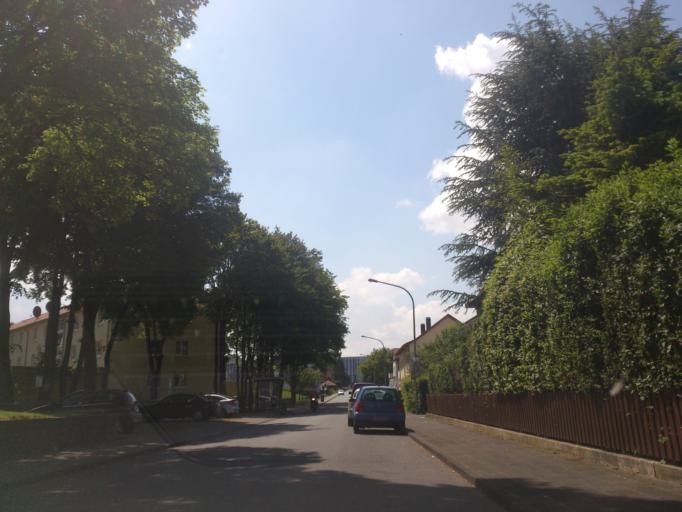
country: DE
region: North Rhine-Westphalia
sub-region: Regierungsbezirk Detmold
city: Paderborn
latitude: 51.7081
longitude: 8.7406
